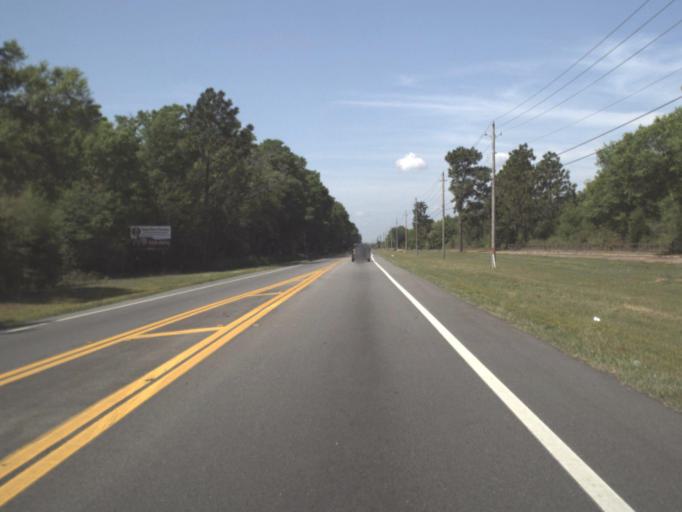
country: US
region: Florida
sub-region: Santa Rosa County
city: East Milton
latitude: 30.6292
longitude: -86.9980
